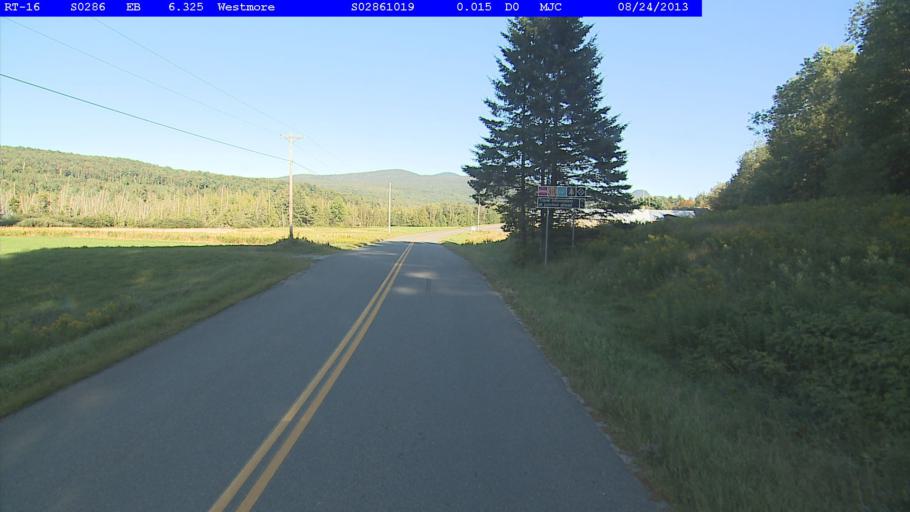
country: US
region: Vermont
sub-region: Orleans County
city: Newport
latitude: 44.7813
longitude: -72.0824
